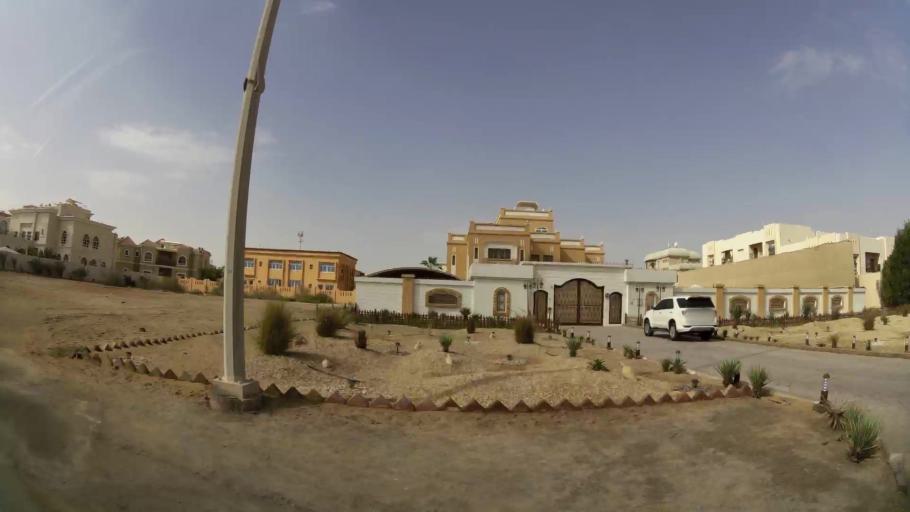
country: AE
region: Abu Dhabi
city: Abu Dhabi
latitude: 24.4232
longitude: 54.5605
